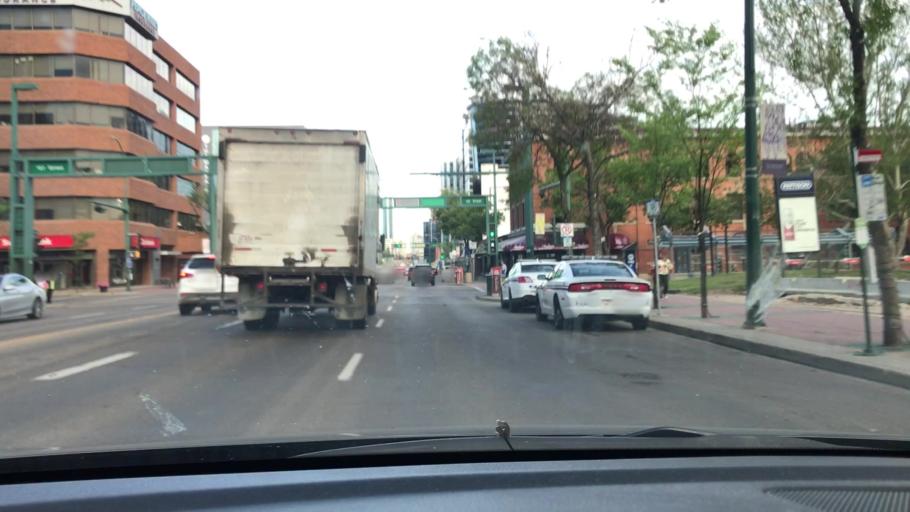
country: CA
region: Alberta
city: Edmonton
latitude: 53.5409
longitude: -113.5040
